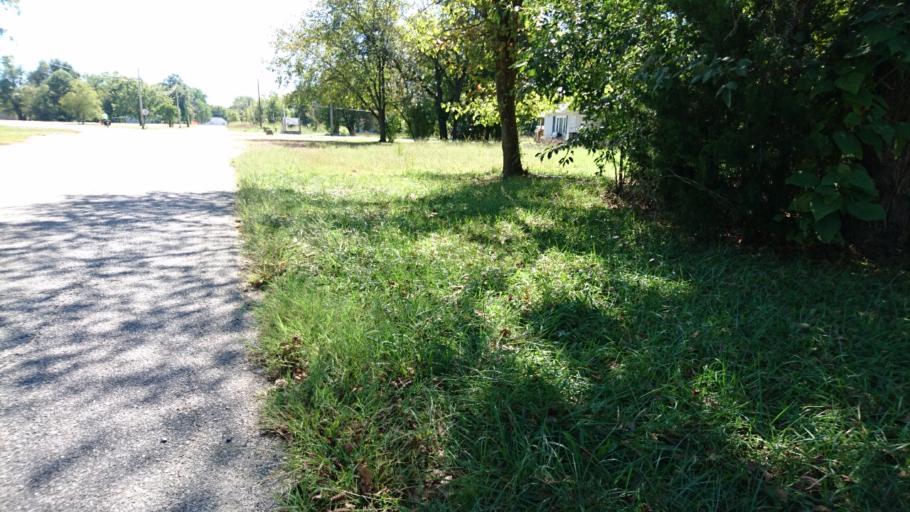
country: US
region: Kansas
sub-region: Cherokee County
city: Baxter Springs
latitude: 37.0350
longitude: -94.7406
